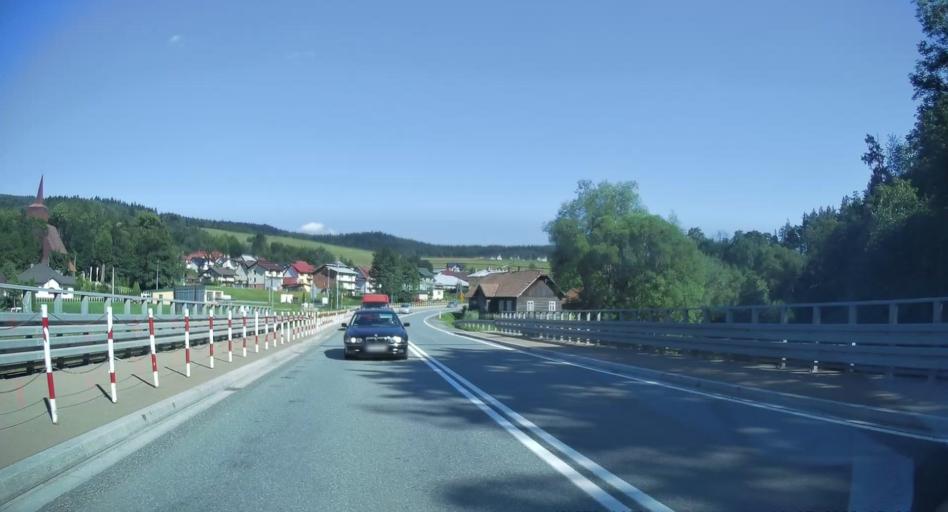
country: PL
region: Lesser Poland Voivodeship
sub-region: Powiat nowosadecki
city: Labowa
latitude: 49.4964
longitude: 20.9061
